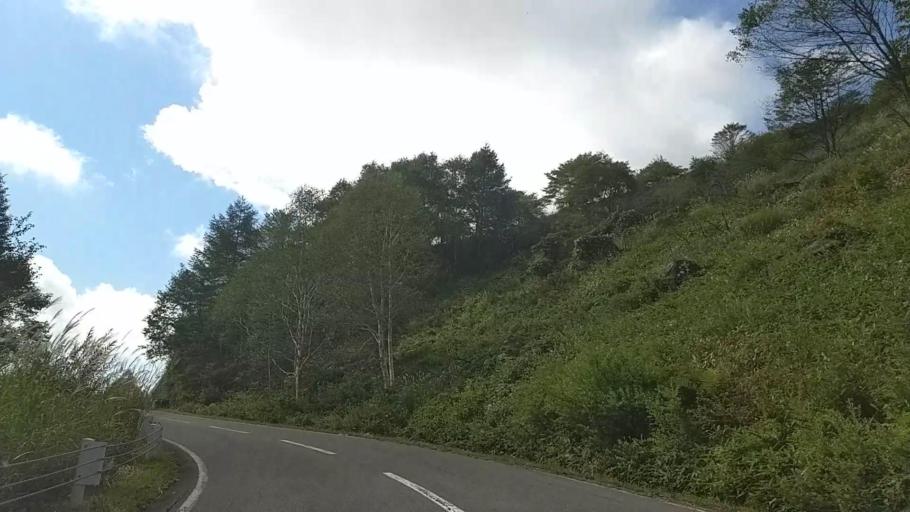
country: JP
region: Nagano
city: Suwa
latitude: 36.0972
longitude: 138.1961
